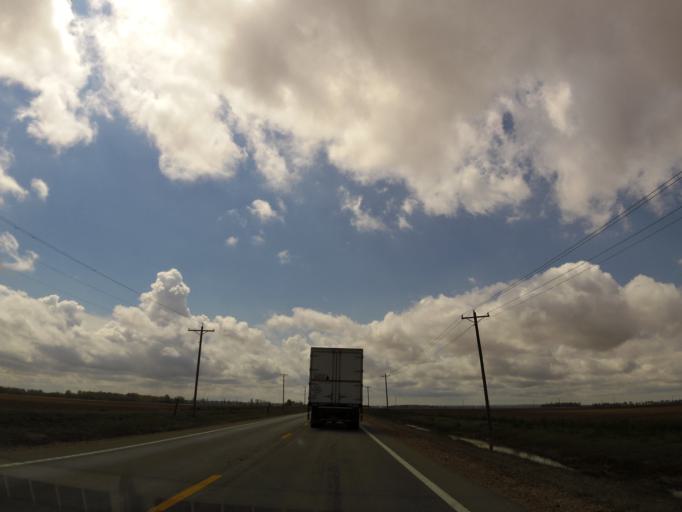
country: US
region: Arkansas
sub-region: Clay County
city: Corning
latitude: 36.3257
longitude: -90.5252
